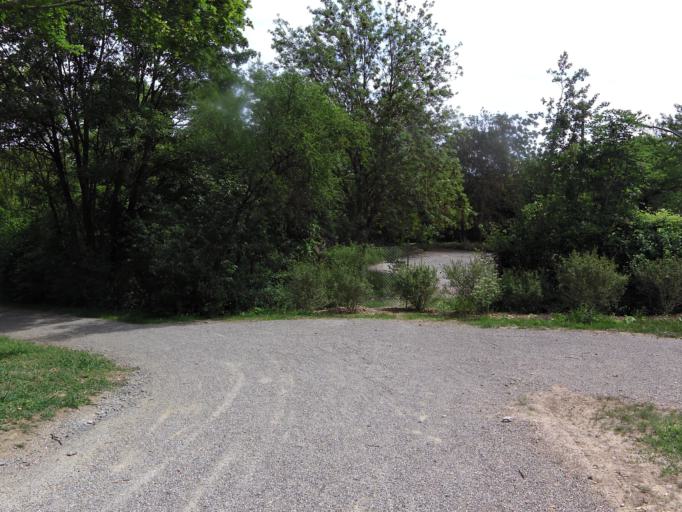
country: DE
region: Bavaria
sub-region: Regierungsbezirk Unterfranken
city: Wuerzburg
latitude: 49.7923
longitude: 9.9705
